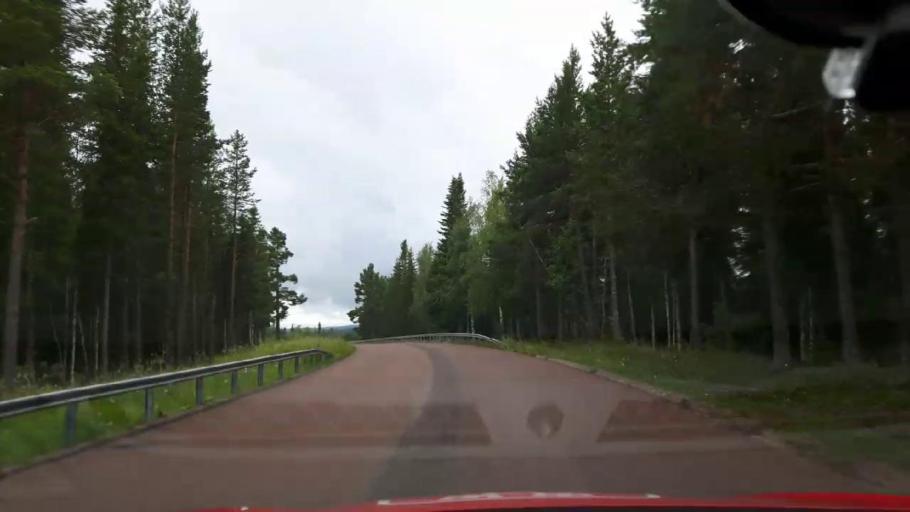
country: SE
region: Jaemtland
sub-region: Krokoms Kommun
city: Valla
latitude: 63.3529
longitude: 13.7243
